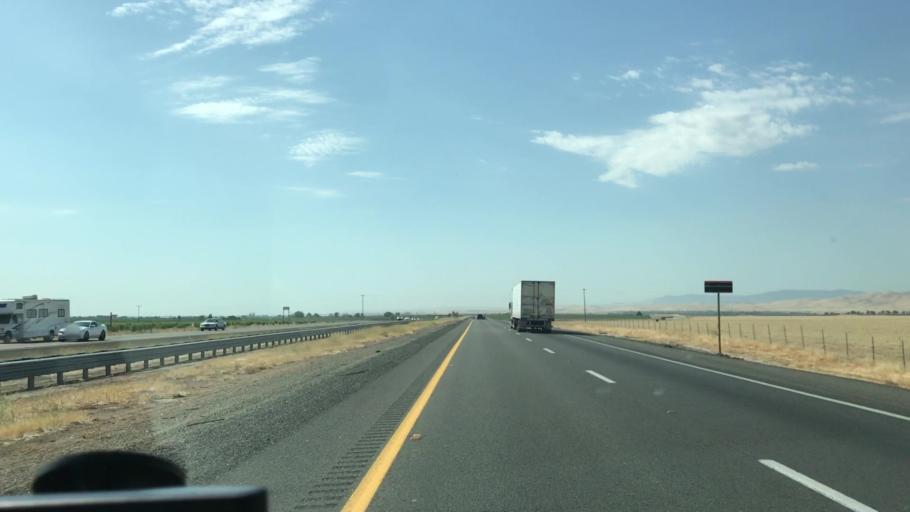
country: US
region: California
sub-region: Merced County
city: Gustine
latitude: 37.1543
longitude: -121.0483
